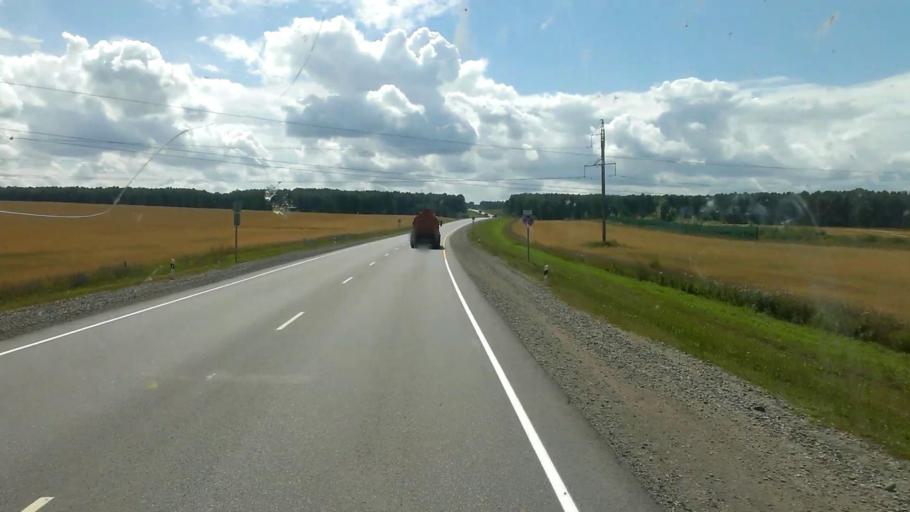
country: RU
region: Altai Krai
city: Troitskoye
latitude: 52.9896
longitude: 84.7428
